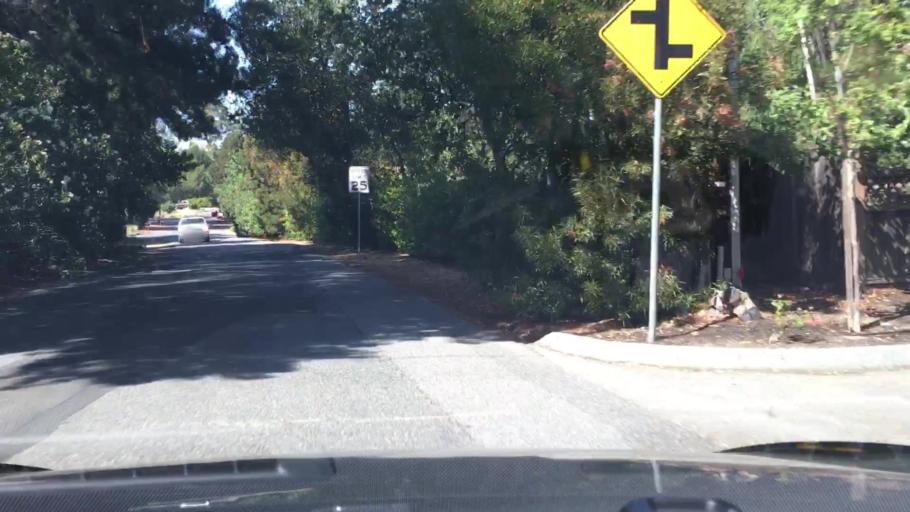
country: US
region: California
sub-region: Santa Clara County
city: Monte Sereno
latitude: 37.2447
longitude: -122.0095
